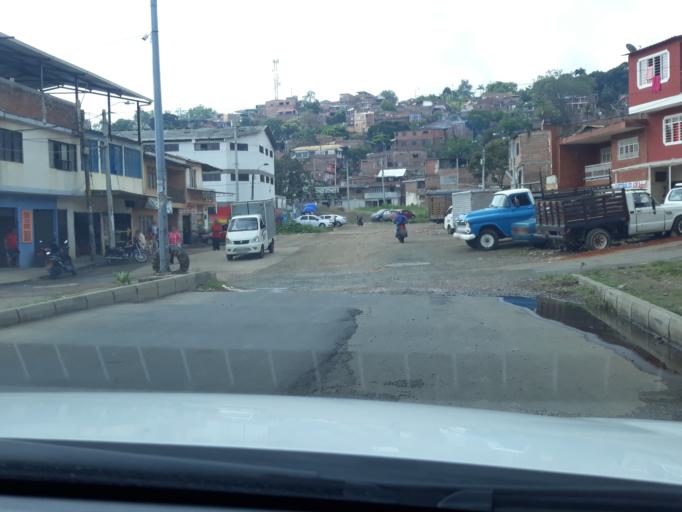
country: CO
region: Valle del Cauca
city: Cali
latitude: 3.3874
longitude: -76.5560
